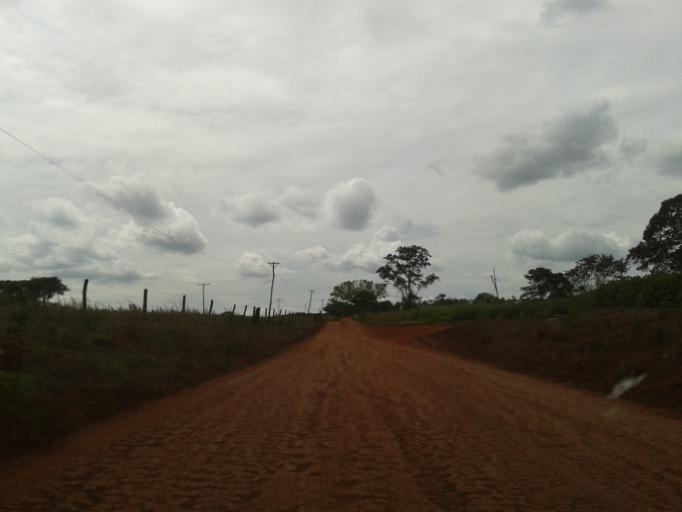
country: BR
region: Minas Gerais
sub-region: Centralina
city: Centralina
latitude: -18.7645
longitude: -49.2210
